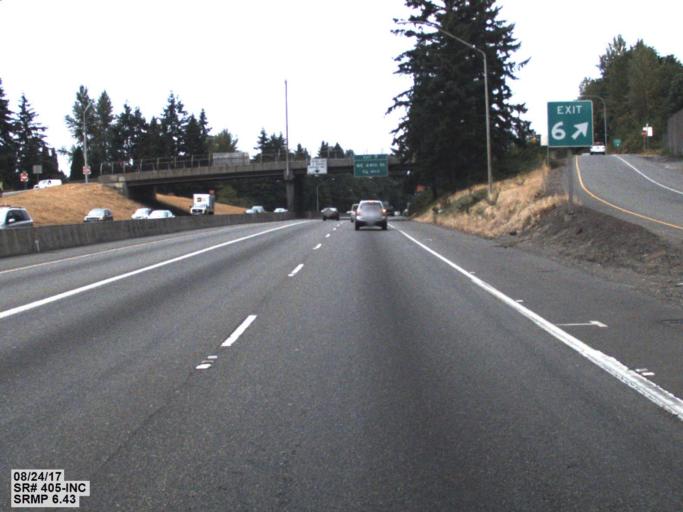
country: US
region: Washington
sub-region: King County
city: Renton
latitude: 47.5173
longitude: -122.1983
